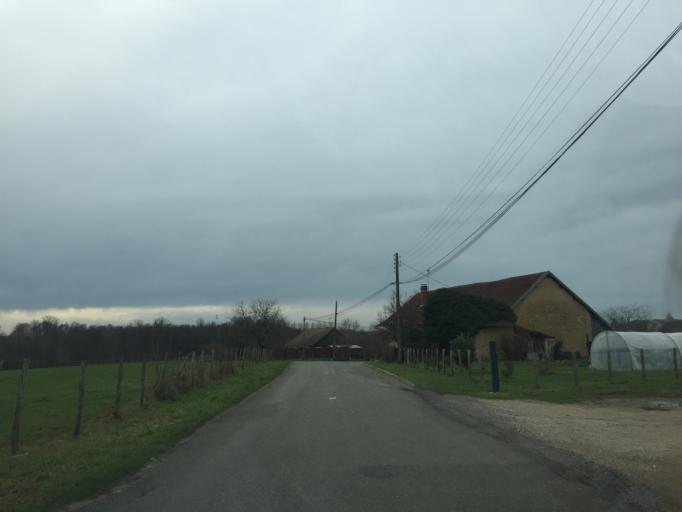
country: FR
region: Franche-Comte
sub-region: Departement du Jura
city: Mont-sous-Vaudrey
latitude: 46.8743
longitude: 5.5349
